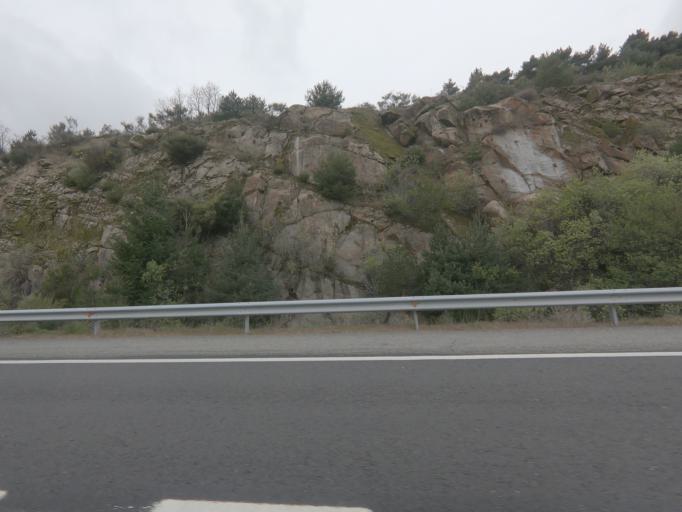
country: ES
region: Castille and Leon
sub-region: Provincia de Salamanca
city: Penacaballera
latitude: 40.3406
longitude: -5.8511
